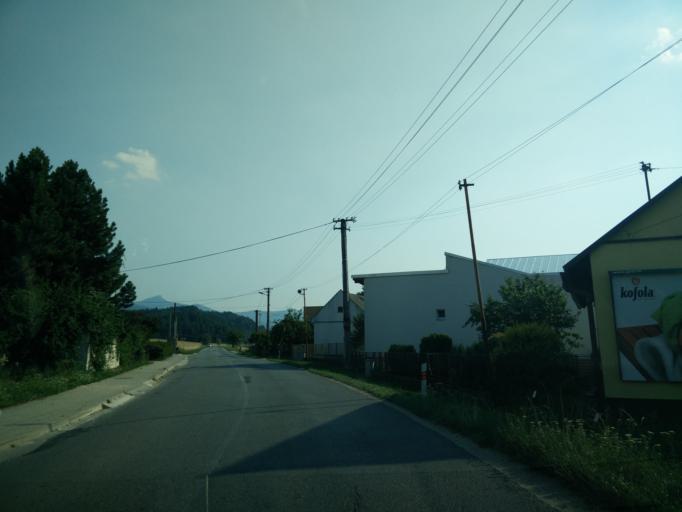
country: SK
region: Zilinsky
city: Rajec
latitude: 49.0672
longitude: 18.6279
